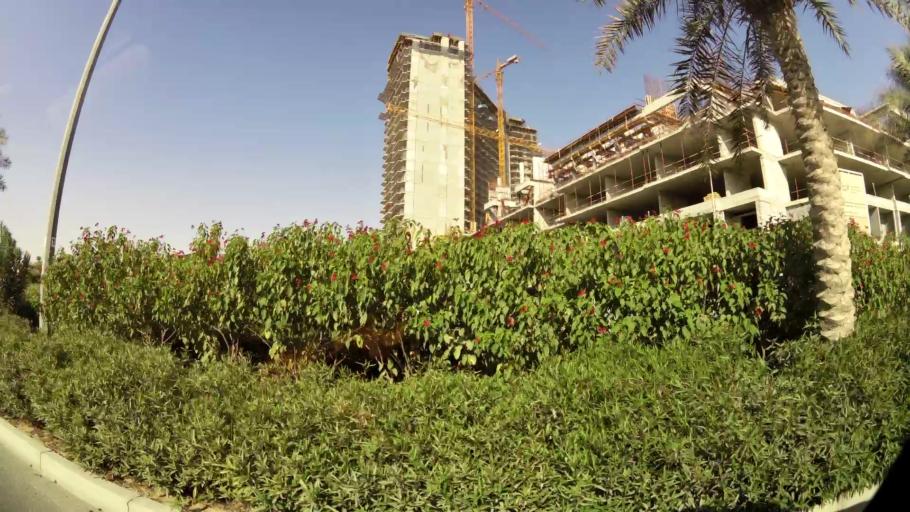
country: AE
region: Dubai
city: Dubai
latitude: 25.0567
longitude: 55.2031
